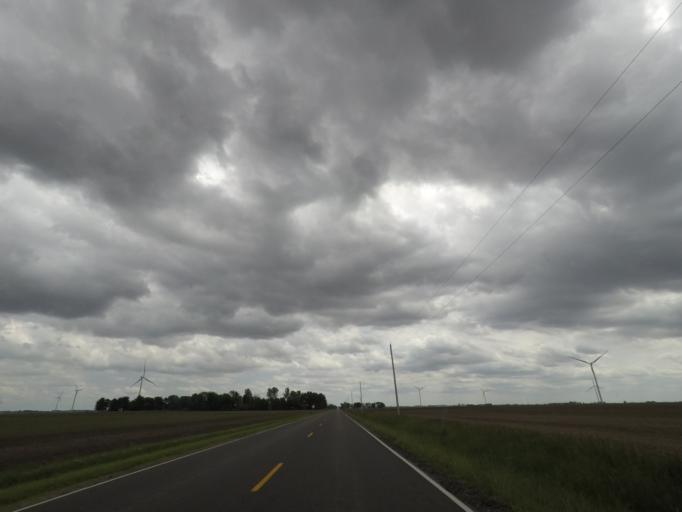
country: US
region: Illinois
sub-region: Macon County
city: Warrensburg
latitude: 39.9903
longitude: -89.0857
